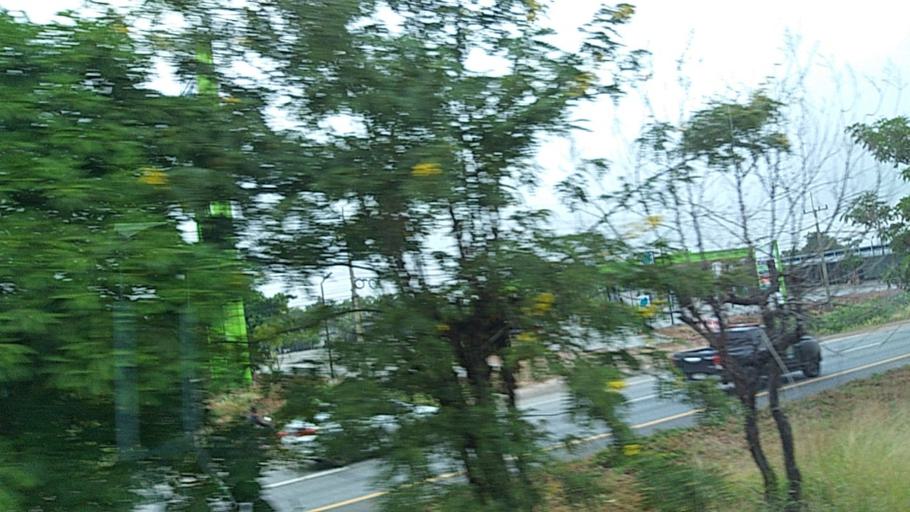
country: TH
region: Nakhon Ratchasima
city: Non Sung
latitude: 15.0975
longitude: 102.2716
